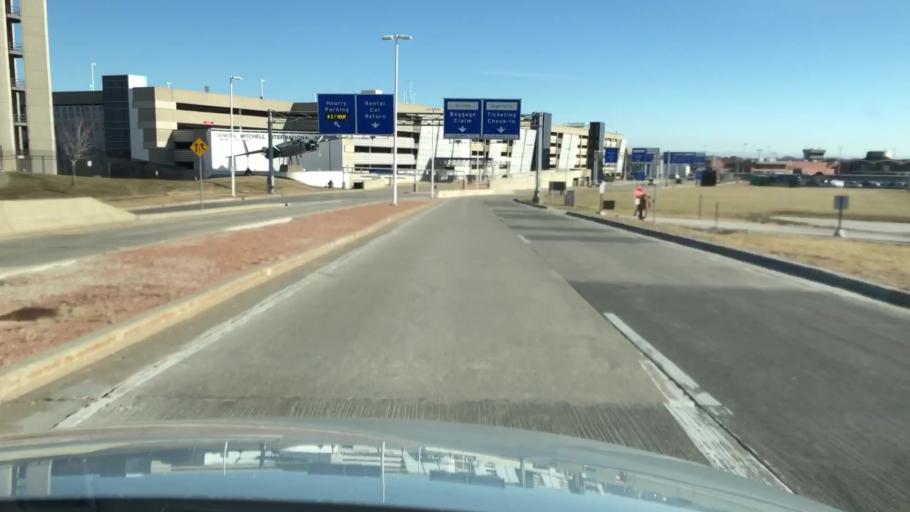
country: US
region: Wisconsin
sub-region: Milwaukee County
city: Saint Francis
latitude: 42.9470
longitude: -87.9075
